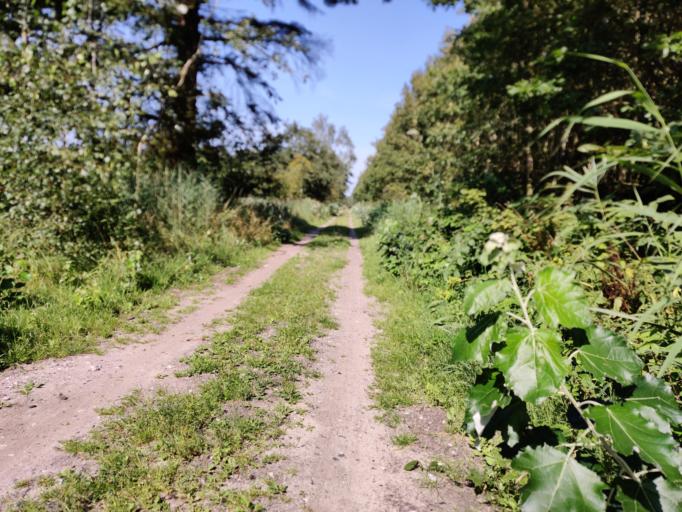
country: DK
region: Zealand
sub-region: Guldborgsund Kommune
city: Nykobing Falster
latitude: 54.6192
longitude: 11.9564
